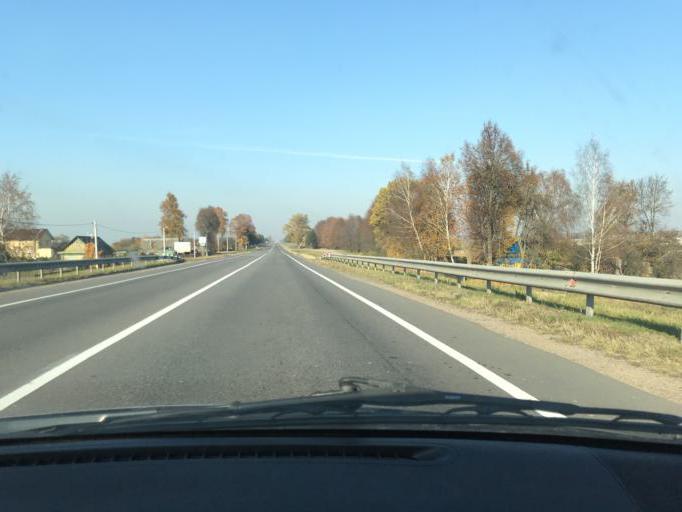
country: BY
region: Mogilev
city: Shklow
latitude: 54.2549
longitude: 30.4506
